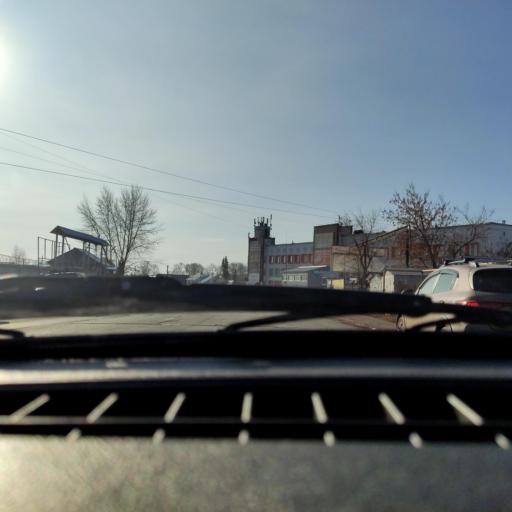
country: RU
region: Bashkortostan
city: Ufa
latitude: 54.8267
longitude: 56.0920
